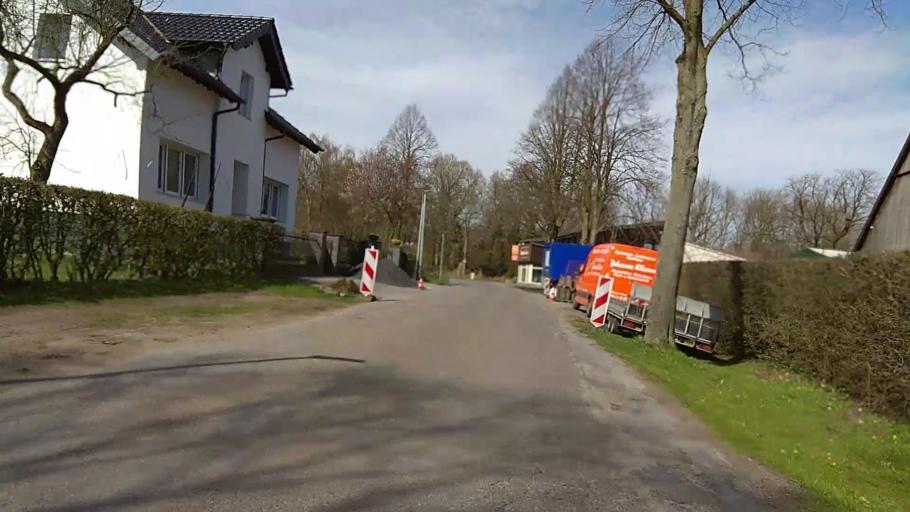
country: DE
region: North Rhine-Westphalia
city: Herten
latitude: 51.5754
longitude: 7.0939
